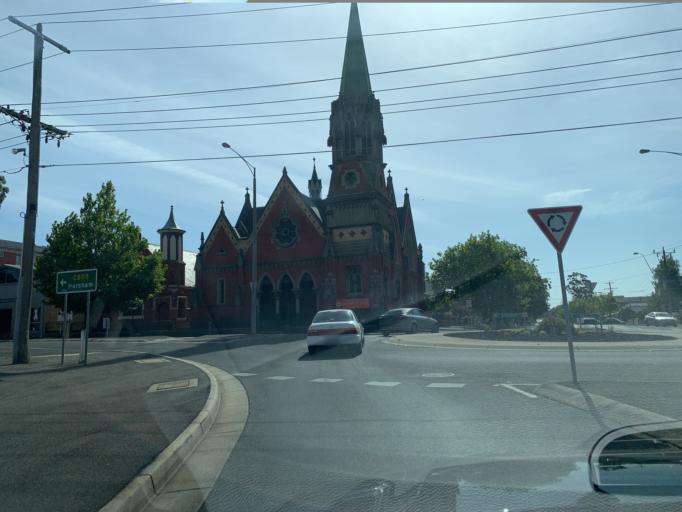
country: AU
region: Victoria
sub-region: Ballarat North
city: Ballarat Central
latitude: -37.5593
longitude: 143.8541
